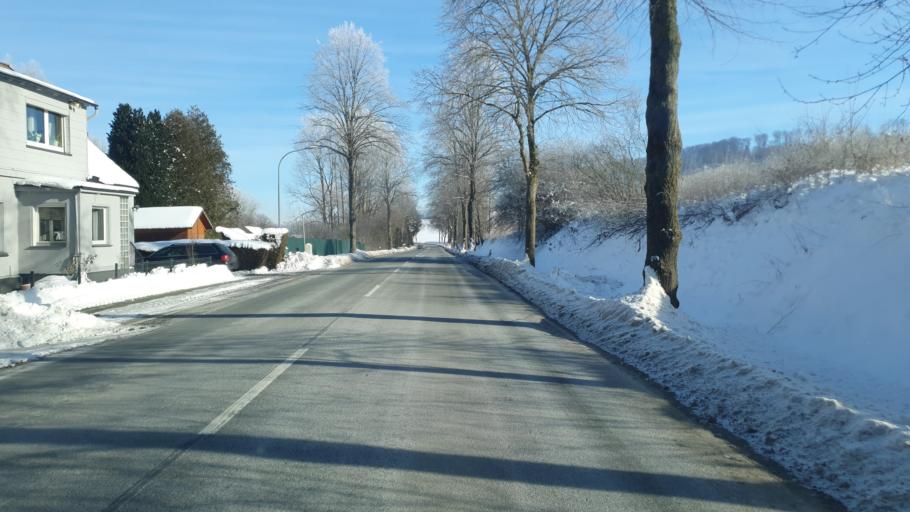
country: DE
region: Lower Saxony
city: Bad Pyrmont
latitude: 52.0167
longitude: 9.2163
